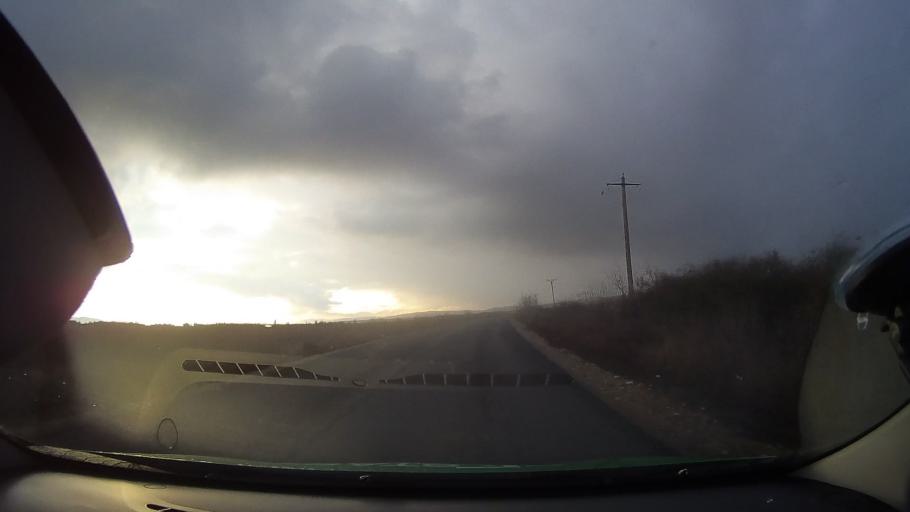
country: RO
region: Cluj
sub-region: Comuna Luna
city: Luncani
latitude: 46.4491
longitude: 23.9470
